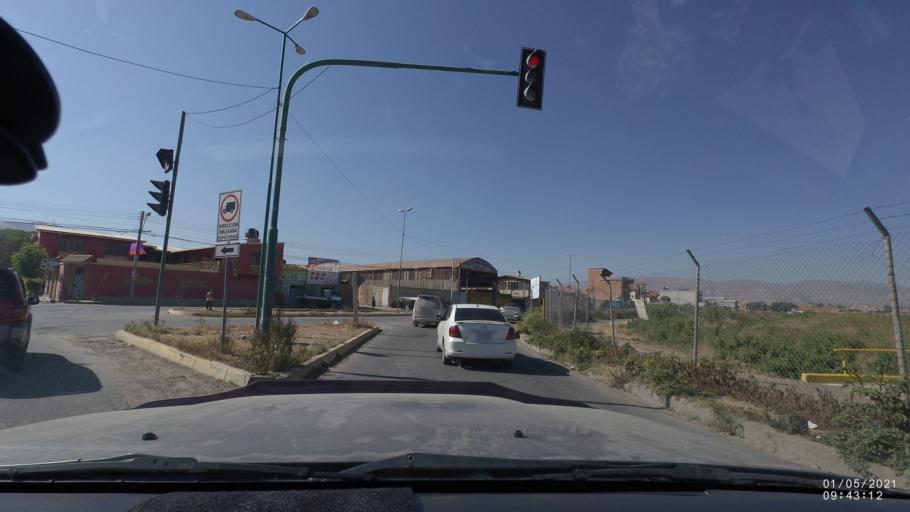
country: BO
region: Cochabamba
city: Cochabamba
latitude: -17.4299
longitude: -66.1630
